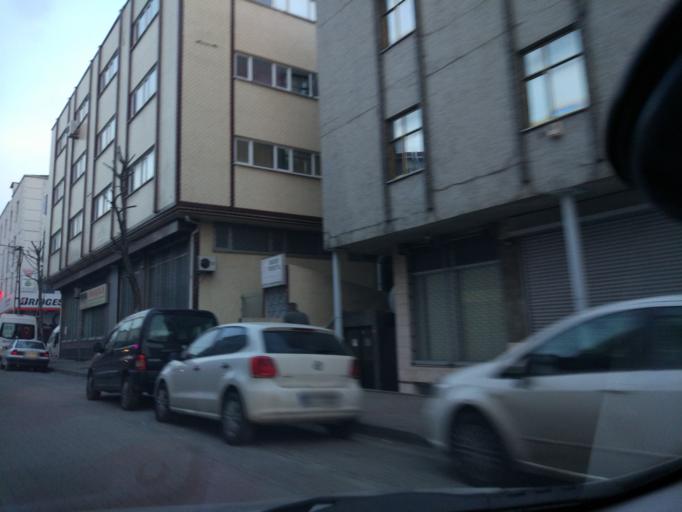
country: TR
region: Istanbul
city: Bahcelievler
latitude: 41.0103
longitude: 28.8279
